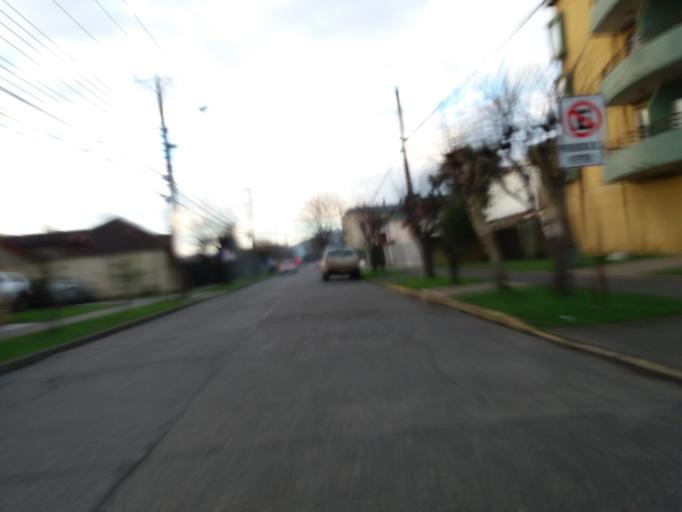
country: CL
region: Araucania
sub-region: Provincia de Cautin
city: Temuco
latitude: -38.7387
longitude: -72.6052
